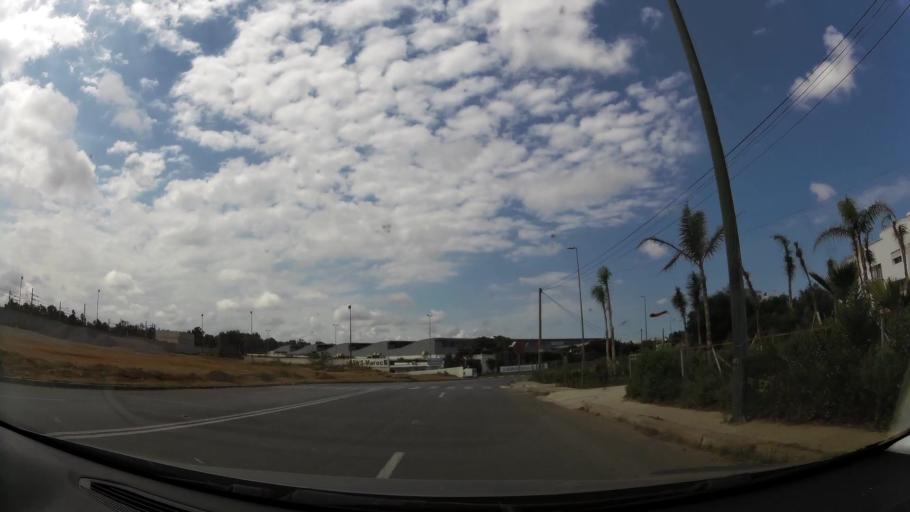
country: MA
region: Gharb-Chrarda-Beni Hssen
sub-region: Kenitra Province
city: Kenitra
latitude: 34.2430
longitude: -6.5985
